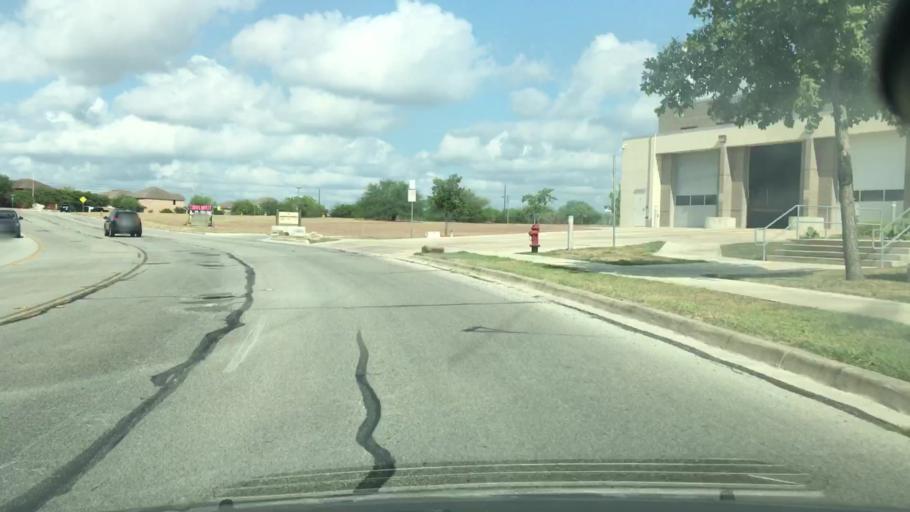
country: US
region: Texas
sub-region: Guadalupe County
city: Northcliff
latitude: 29.5948
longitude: -98.2523
